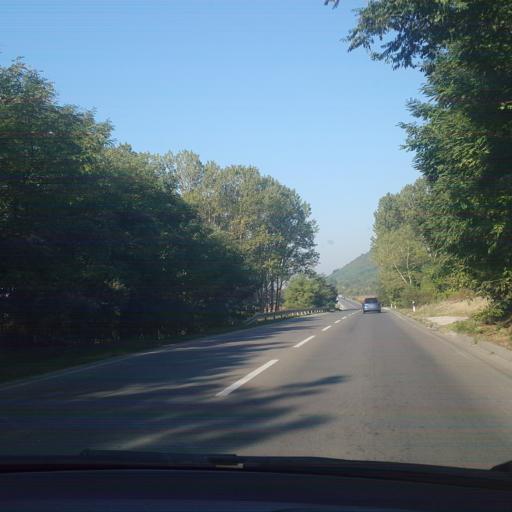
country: RS
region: Central Serbia
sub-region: Toplicki Okrug
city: Prokuplje
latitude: 43.2334
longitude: 21.5289
